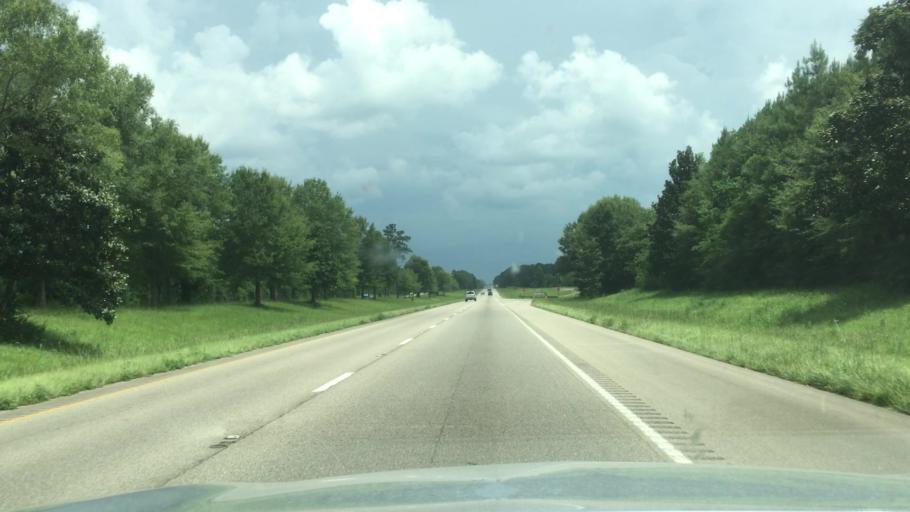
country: US
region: Mississippi
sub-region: Pearl River County
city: Picayune
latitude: 30.5595
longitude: -89.6405
